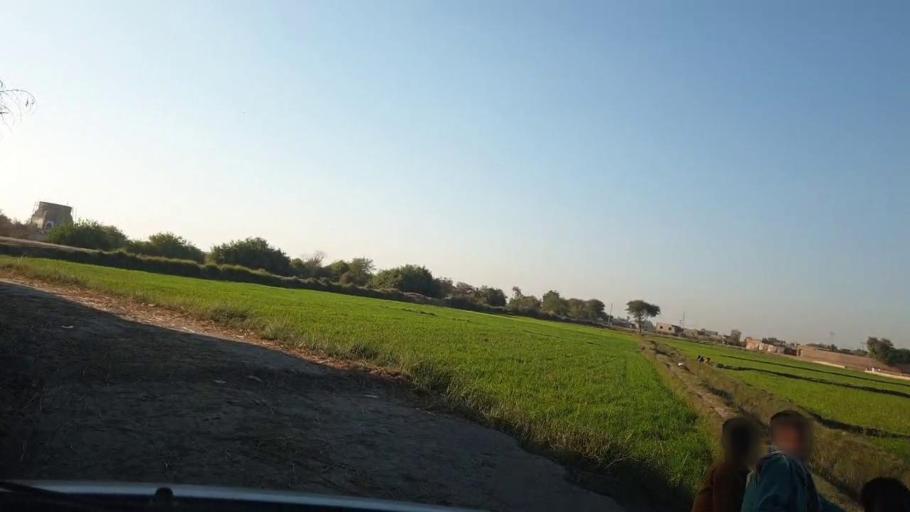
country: PK
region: Sindh
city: Khairpur Nathan Shah
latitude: 27.0428
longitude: 67.7280
